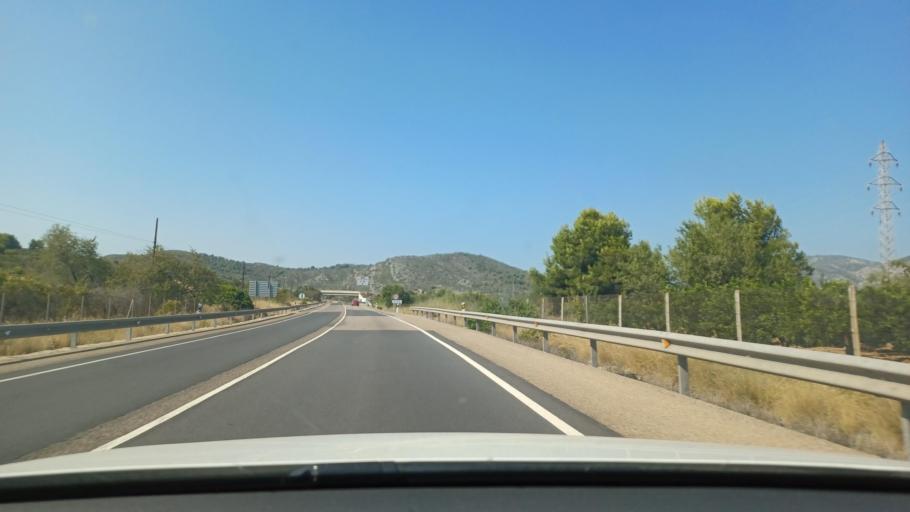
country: ES
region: Valencia
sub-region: Provincia de Castello
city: Alcala de Xivert
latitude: 40.2639
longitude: 0.2399
